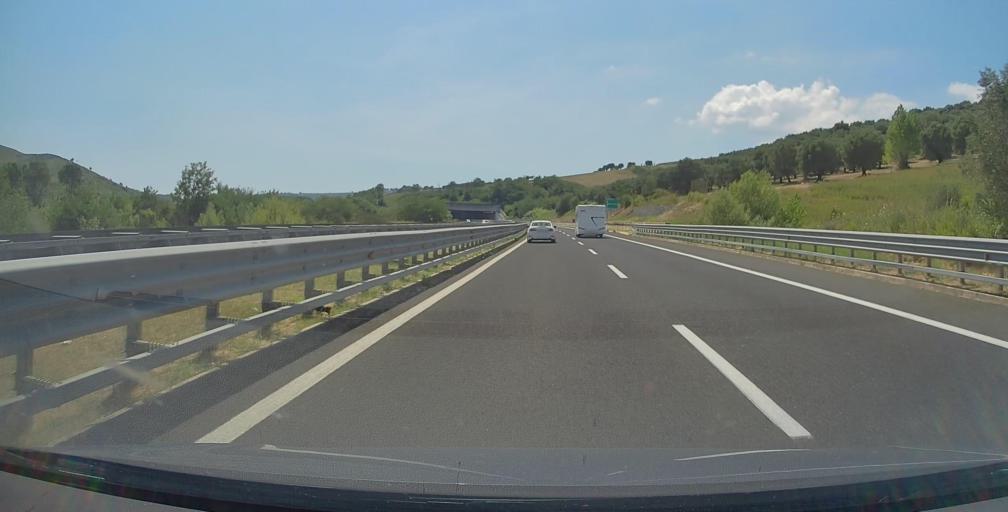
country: IT
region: Calabria
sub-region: Provincia di Vibo-Valentia
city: Paravati
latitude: 38.5734
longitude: 16.0975
